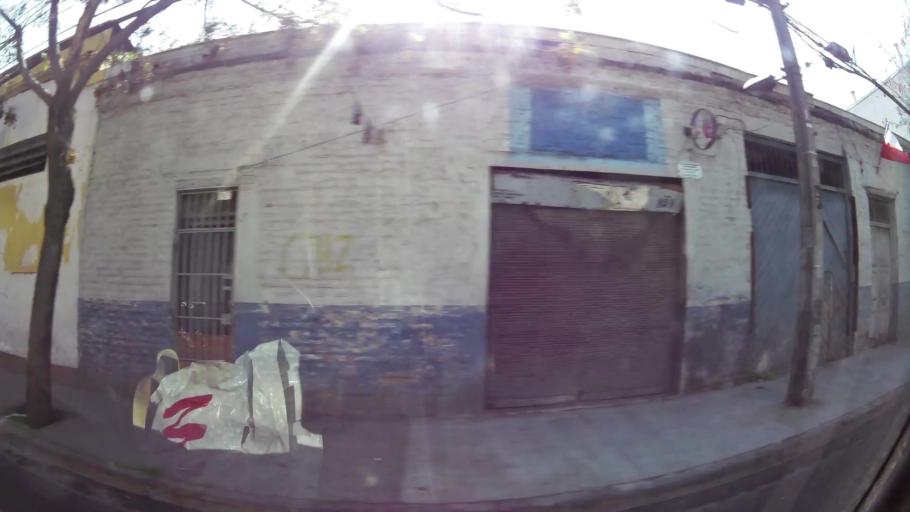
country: CL
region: Santiago Metropolitan
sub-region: Provincia de Santiago
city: Santiago
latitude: -33.4719
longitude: -70.6463
